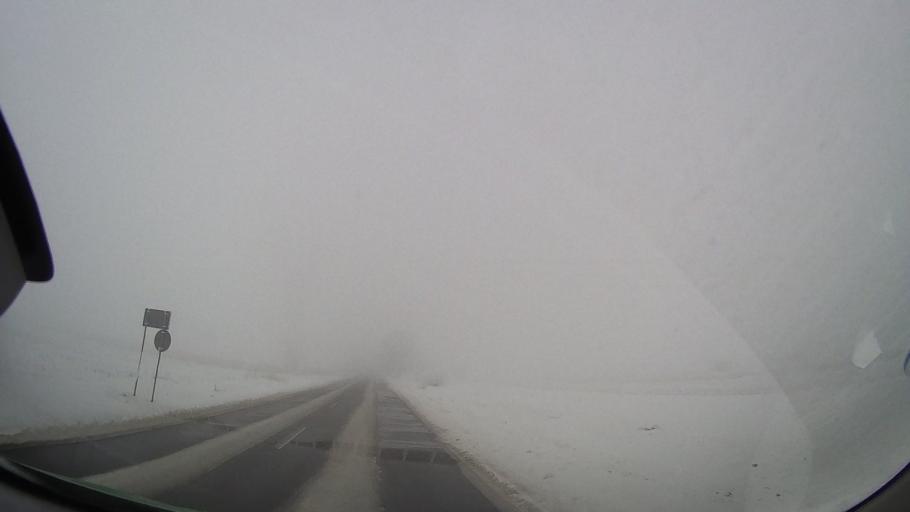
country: RO
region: Neamt
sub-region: Comuna Sabaoani
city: Sabaoani
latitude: 47.0312
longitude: 26.8574
